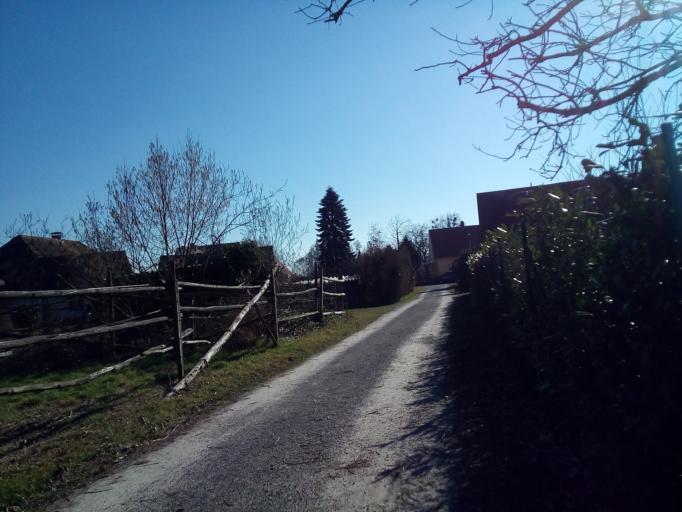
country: DE
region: Baden-Wuerttemberg
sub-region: Karlsruhe Region
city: Schwarzach
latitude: 48.7354
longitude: 8.0568
